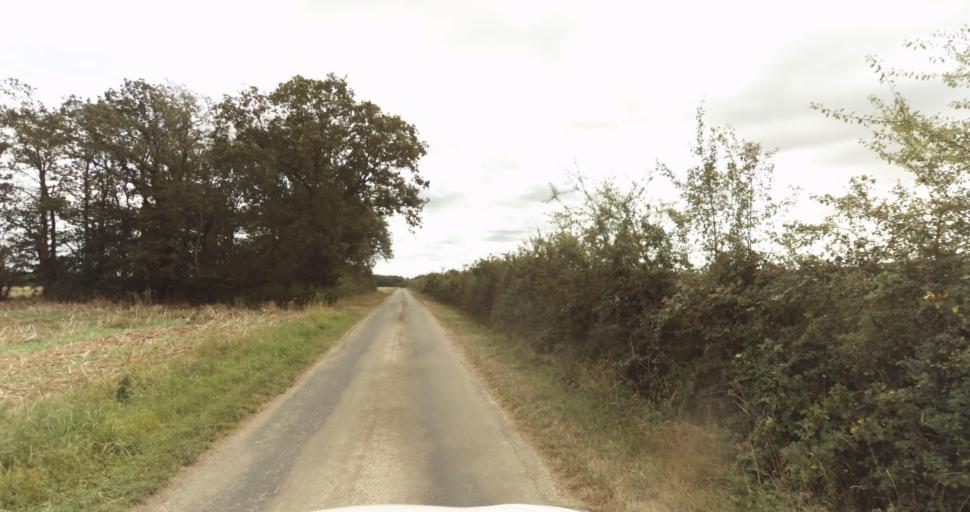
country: FR
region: Haute-Normandie
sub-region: Departement de l'Eure
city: Tillieres-sur-Avre
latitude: 48.7831
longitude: 1.1059
